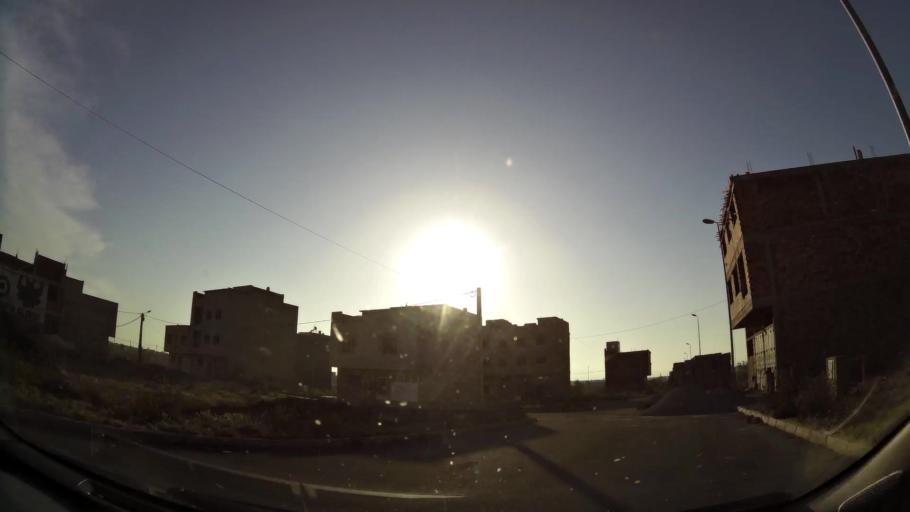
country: MA
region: Oriental
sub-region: Oujda-Angad
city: Oujda
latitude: 34.7088
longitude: -1.9010
